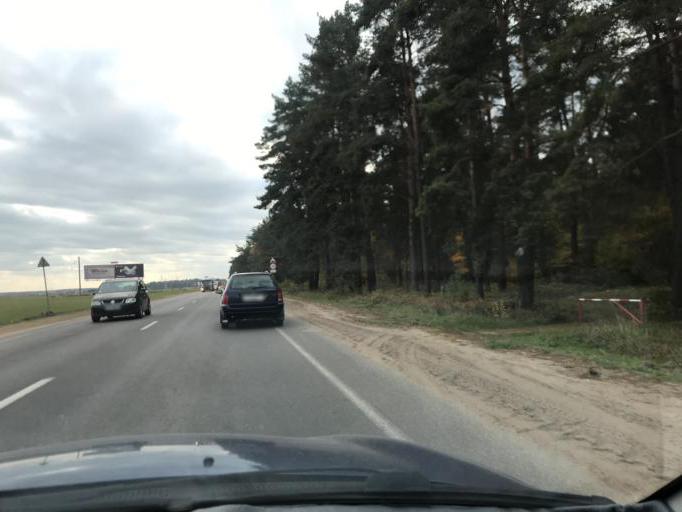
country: BY
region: Grodnenskaya
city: Lida
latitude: 53.8843
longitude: 25.2549
